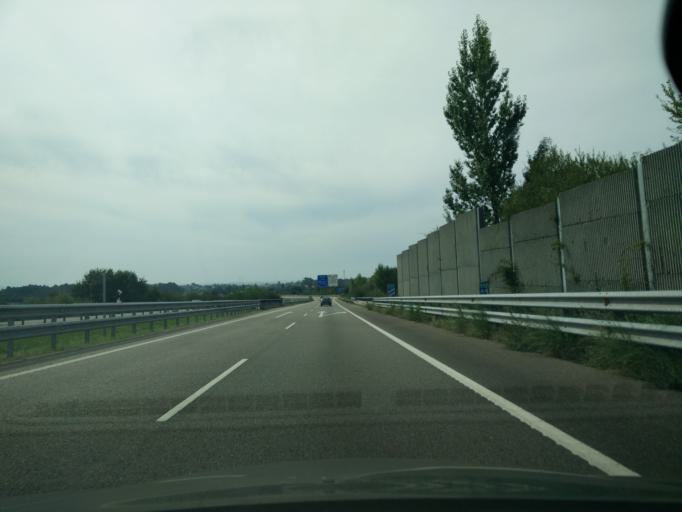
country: ES
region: Asturias
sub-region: Province of Asturias
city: Arriba
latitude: 43.5103
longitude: -5.5618
